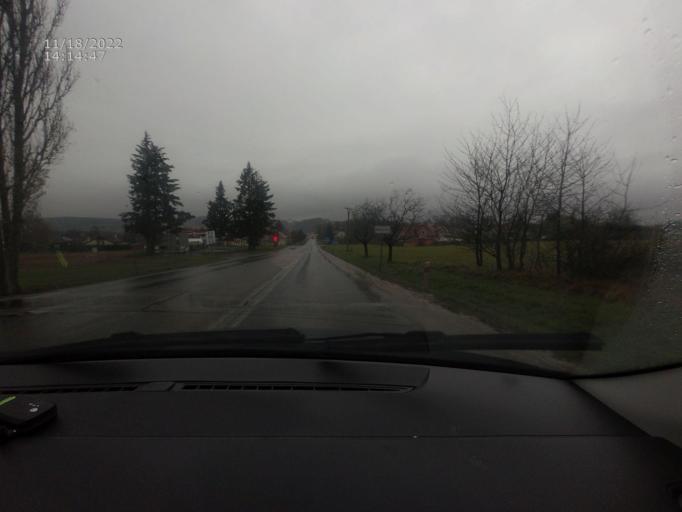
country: CZ
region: Jihocesky
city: Mirotice
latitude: 49.4232
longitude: 14.0361
